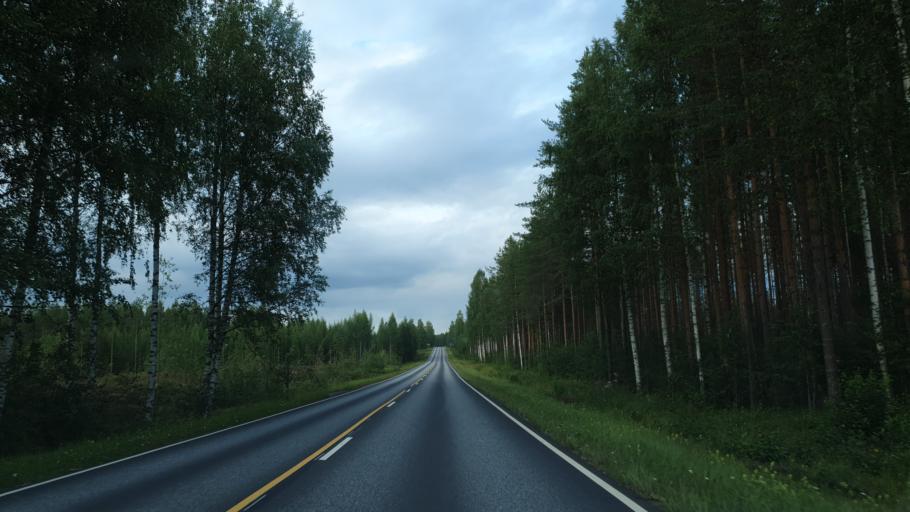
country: FI
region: North Karelia
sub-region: Joensuu
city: Eno
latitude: 63.0346
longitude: 30.1065
